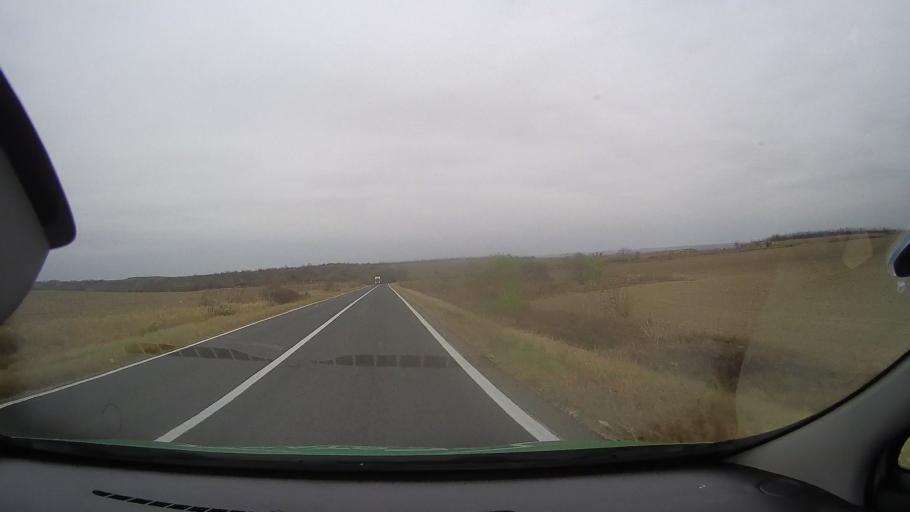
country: RO
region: Constanta
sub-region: Comuna Garliciu
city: Garliciu
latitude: 44.7106
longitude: 28.0813
